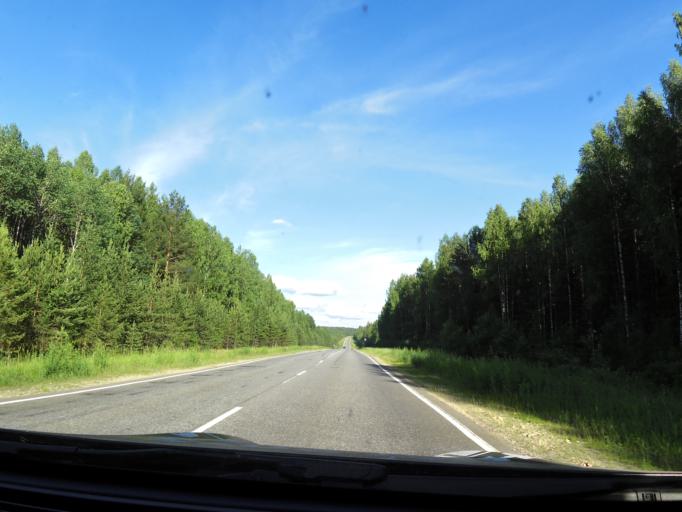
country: RU
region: Kirov
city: Chernaya Kholunitsa
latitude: 58.8272
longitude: 51.7771
